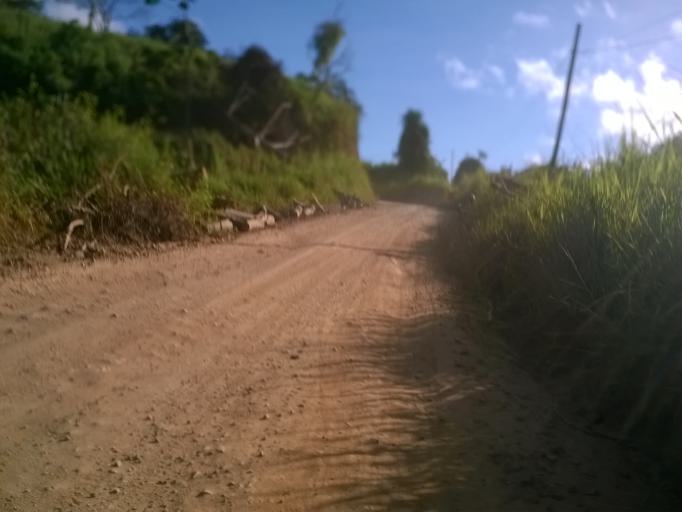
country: BR
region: Minas Gerais
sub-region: Uba
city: Uba
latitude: -21.0821
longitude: -42.9821
